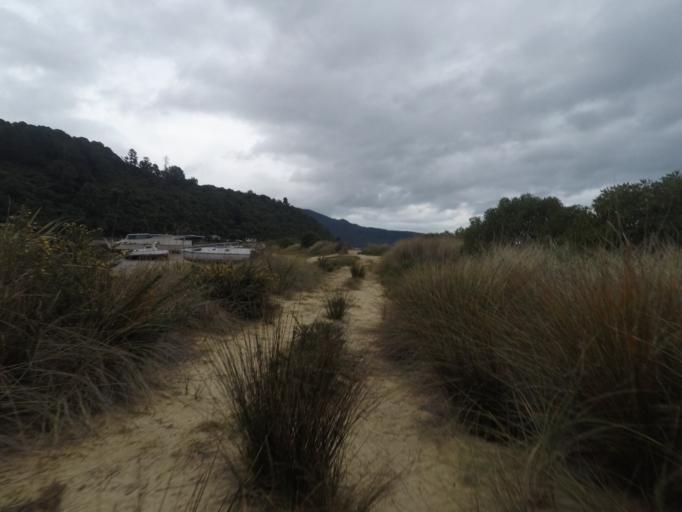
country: NZ
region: Tasman
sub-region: Tasman District
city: Motueka
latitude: -41.0120
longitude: 173.0071
